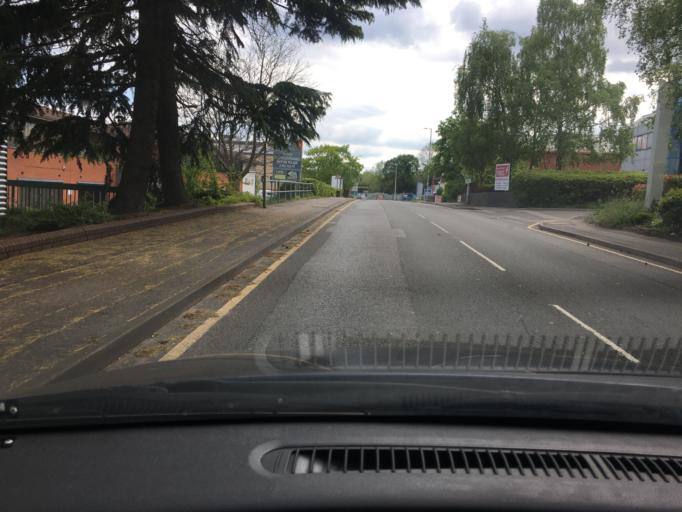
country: GB
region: England
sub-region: Bracknell Forest
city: Bracknell
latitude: 51.4158
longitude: -0.7624
